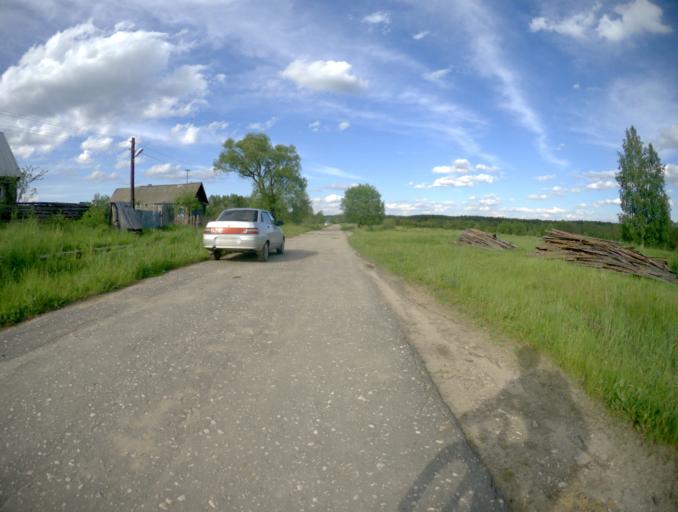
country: RU
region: Vladimir
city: Velikodvorskiy
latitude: 55.3749
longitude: 40.8644
